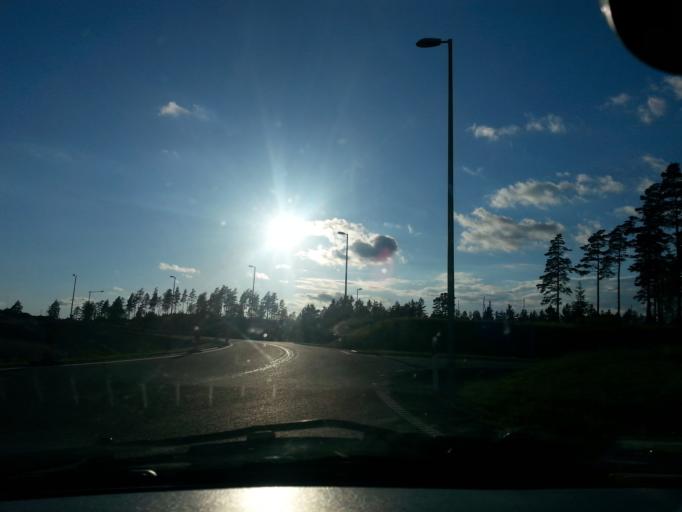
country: SE
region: Joenkoeping
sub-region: Gislaveds Kommun
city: Gislaved
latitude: 57.3238
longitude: 13.5469
